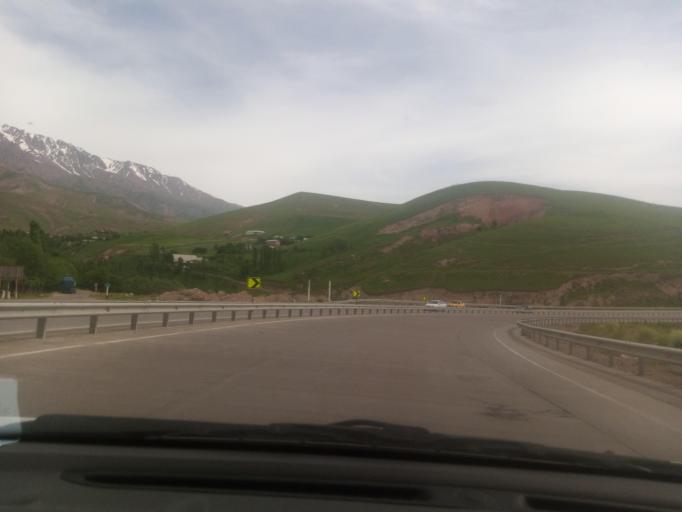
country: UZ
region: Toshkent
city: Angren
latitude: 41.0672
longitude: 70.2203
